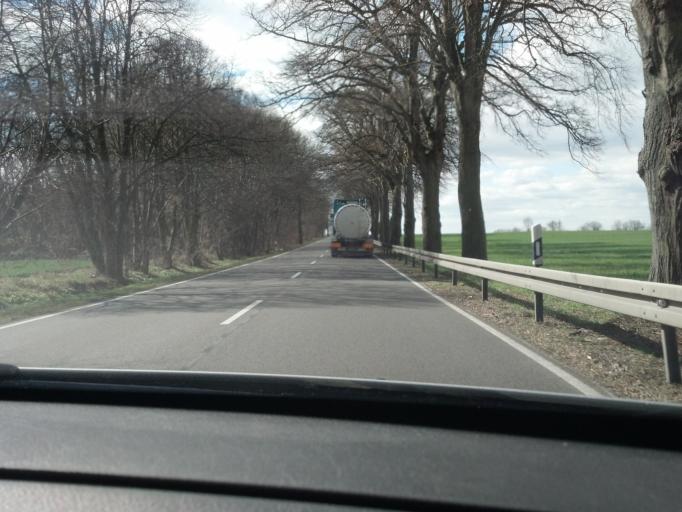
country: DE
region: Mecklenburg-Vorpommern
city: Rechlin
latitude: 53.3148
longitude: 12.7454
